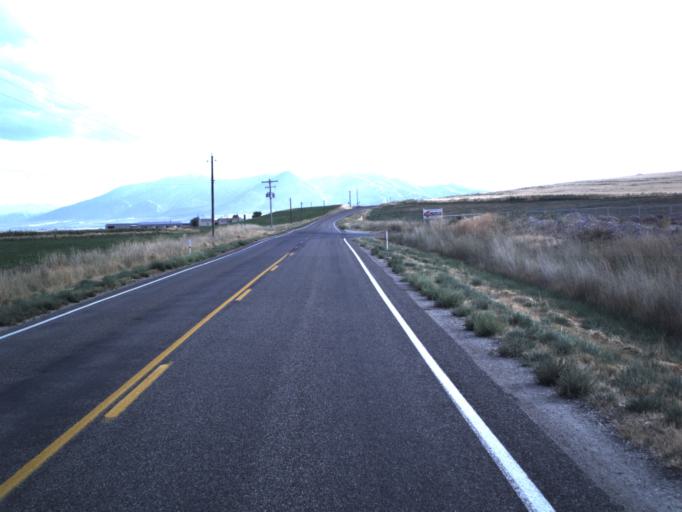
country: US
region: Utah
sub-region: Cache County
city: Benson
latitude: 41.8723
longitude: -111.9494
